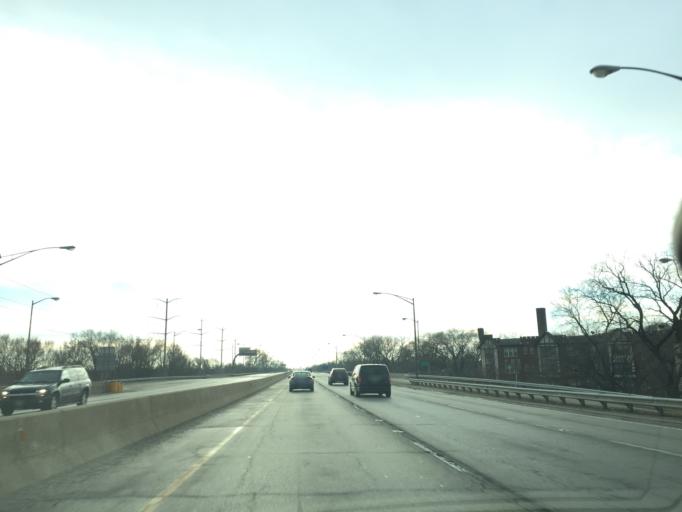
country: US
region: Illinois
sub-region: Cook County
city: Chicago
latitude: 41.7668
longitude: -87.6097
